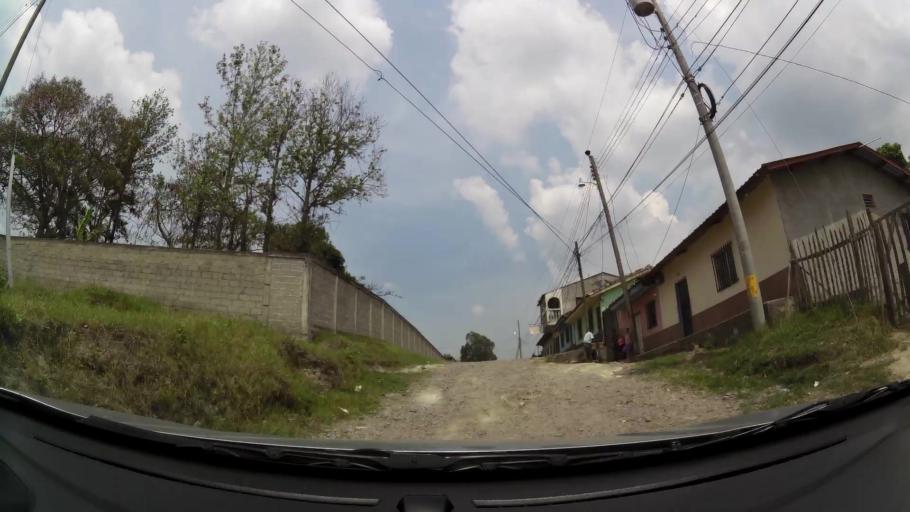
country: HN
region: Comayagua
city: Siguatepeque
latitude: 14.6006
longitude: -87.8284
